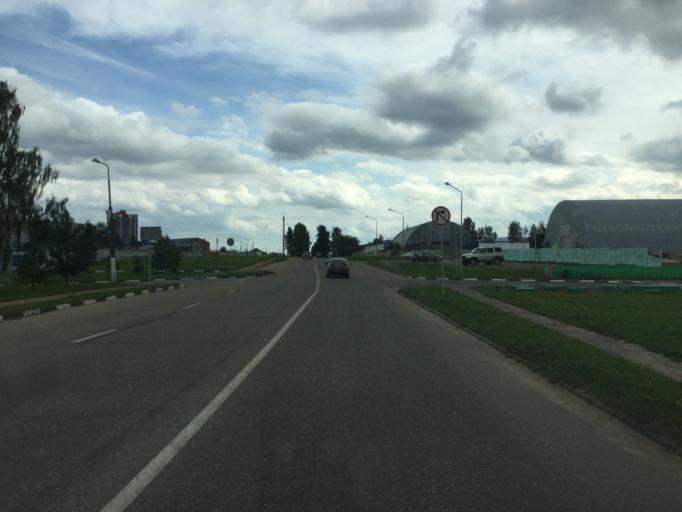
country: BY
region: Vitebsk
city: Vitebsk
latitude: 55.1704
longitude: 30.2485
